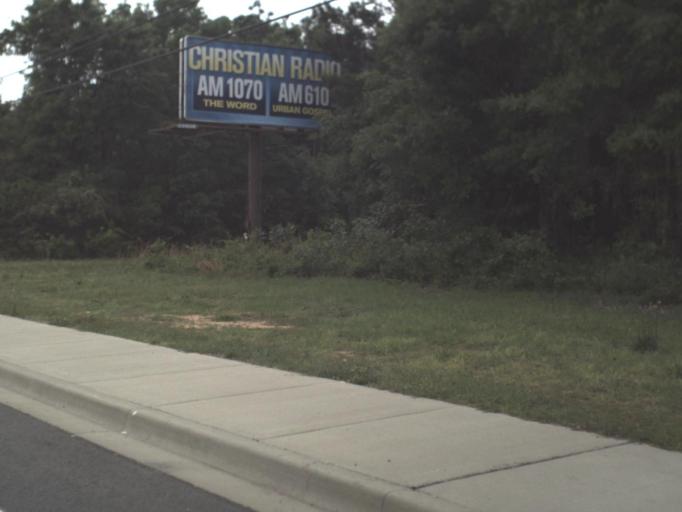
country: US
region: Florida
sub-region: Santa Rosa County
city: Bagdad
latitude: 30.5921
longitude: -87.0821
